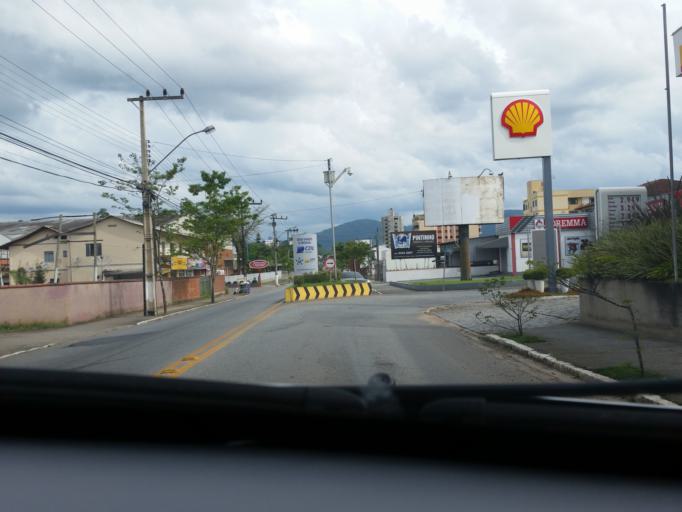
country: BR
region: Santa Catarina
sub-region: Indaial
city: Indaial
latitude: -26.8848
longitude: -49.2460
